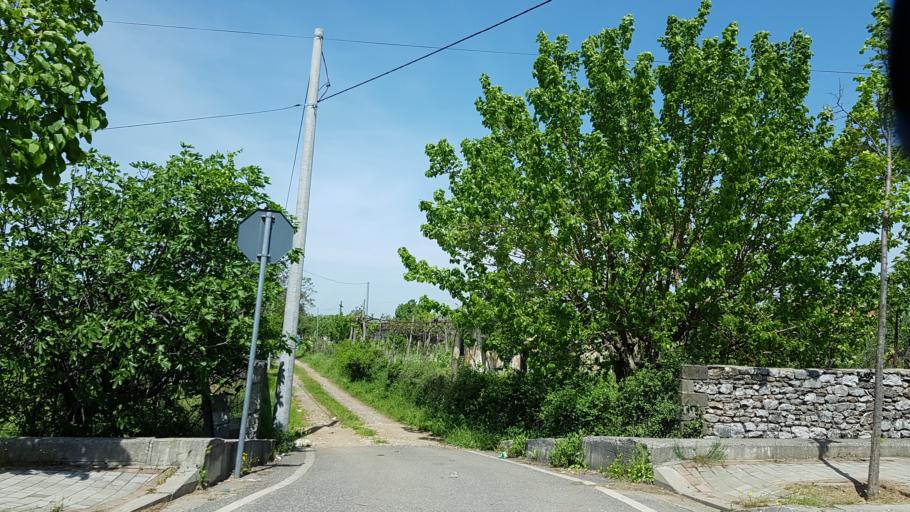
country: AL
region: Shkoder
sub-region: Rrethi i Shkodres
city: Shkoder
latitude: 42.1066
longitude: 19.5605
